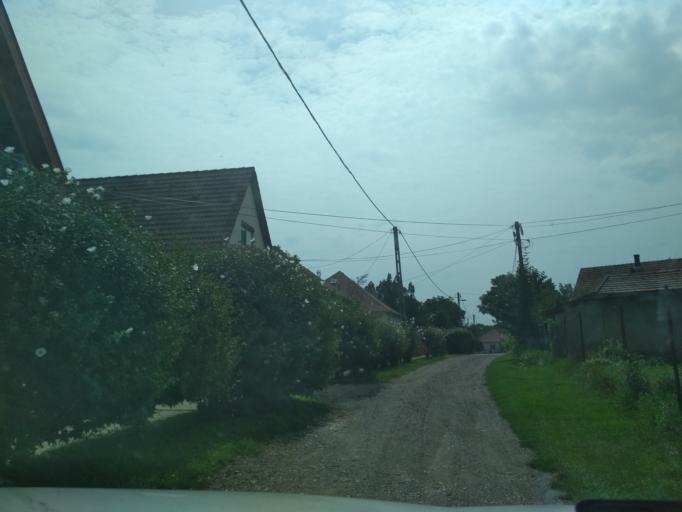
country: HU
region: Jasz-Nagykun-Szolnok
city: Tiszafured
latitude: 47.6115
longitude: 20.7620
